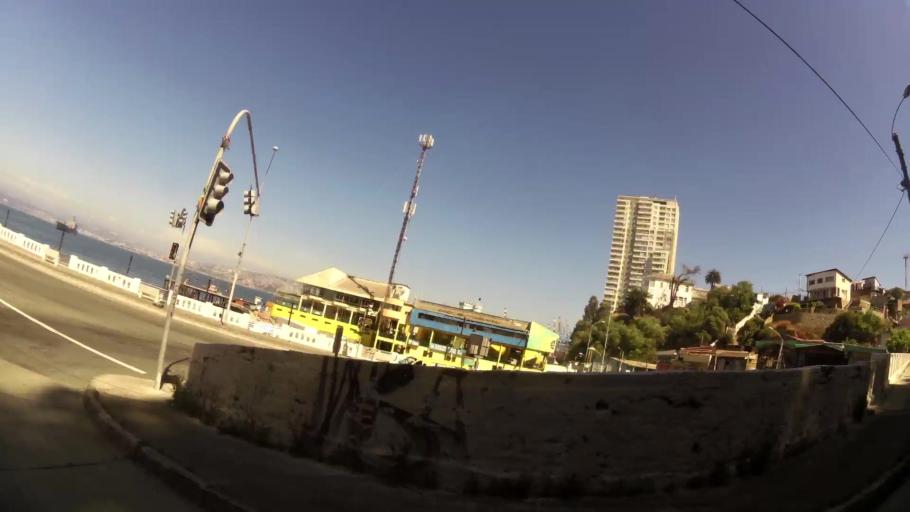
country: CL
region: Valparaiso
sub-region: Provincia de Valparaiso
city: Valparaiso
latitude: -33.0216
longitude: -71.6339
